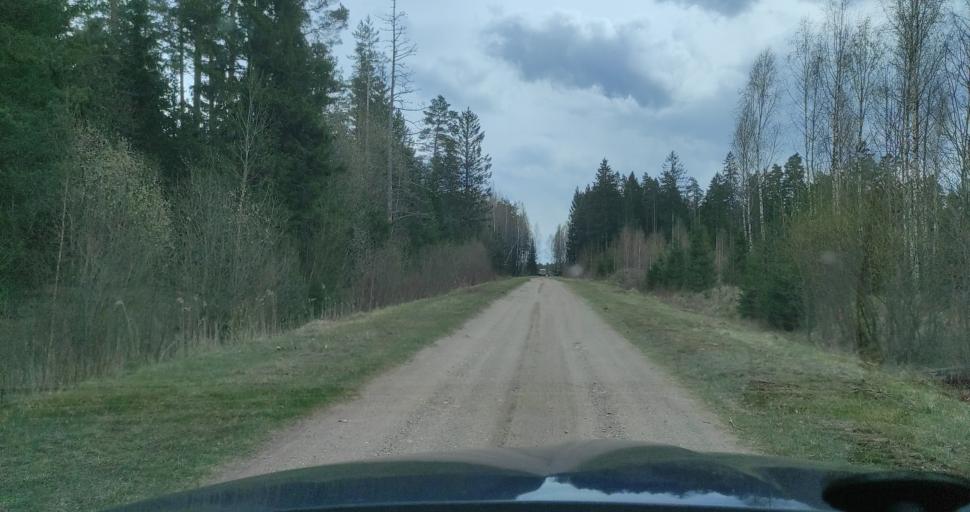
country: LV
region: Dundaga
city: Dundaga
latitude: 57.3590
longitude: 22.1522
